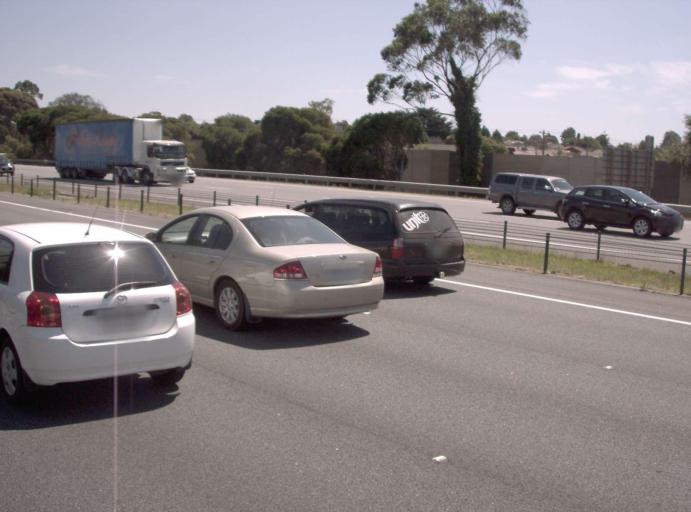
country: AU
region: Victoria
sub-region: Monash
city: Notting Hill
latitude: -37.9147
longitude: 145.1676
